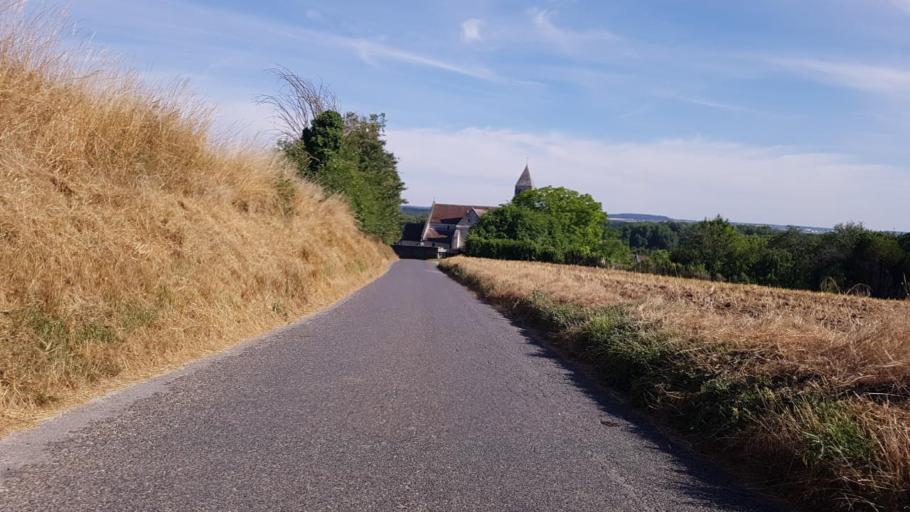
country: FR
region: Picardie
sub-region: Departement de l'Oise
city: Pontpoint
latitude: 49.2982
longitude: 2.6403
